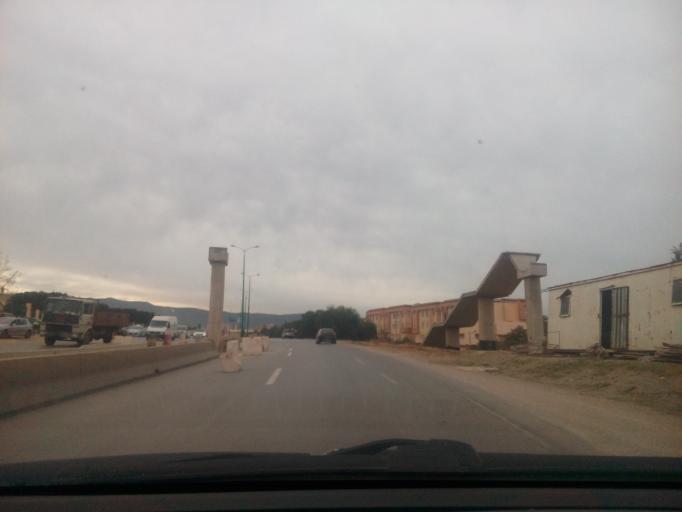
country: DZ
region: Tlemcen
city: Mansoura
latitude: 34.8971
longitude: -1.3552
